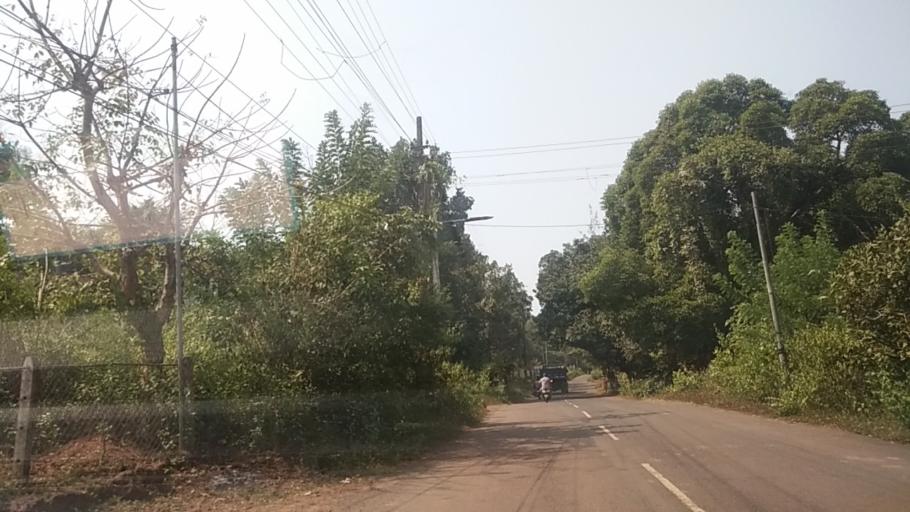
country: IN
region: Goa
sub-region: North Goa
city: Mapuca
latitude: 15.6153
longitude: 73.7982
